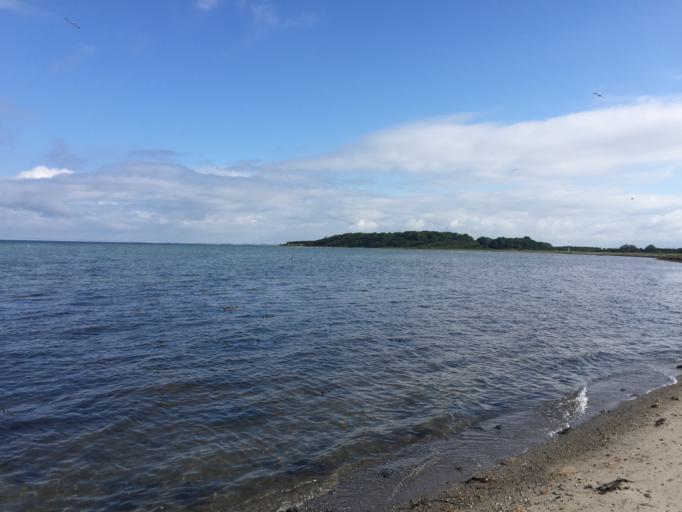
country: DK
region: Zealand
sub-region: Slagelse Kommune
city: Korsor
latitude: 55.2376
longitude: 11.1723
